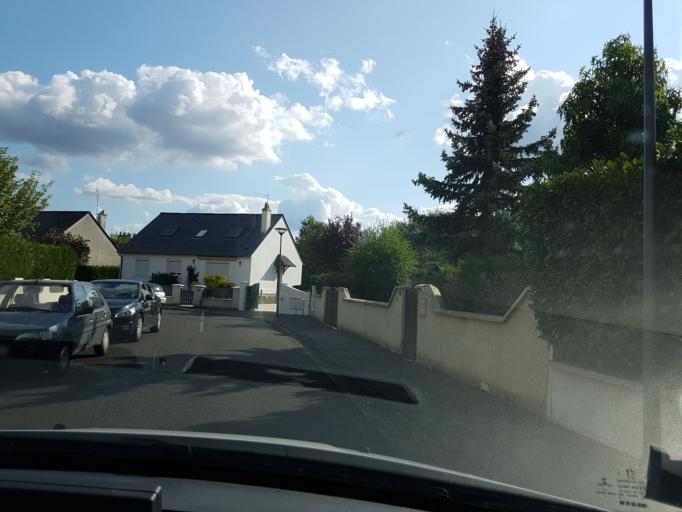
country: FR
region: Centre
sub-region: Departement d'Indre-et-Loire
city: Saint-Avertin
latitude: 47.3640
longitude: 0.7514
